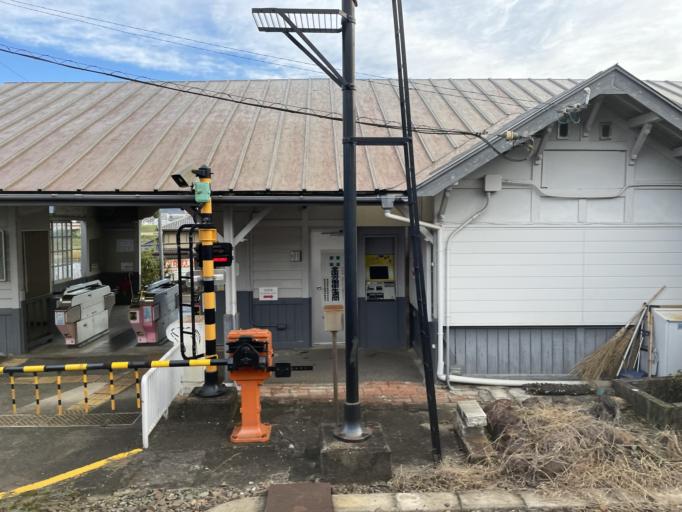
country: JP
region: Wakayama
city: Hashimoto
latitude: 34.2966
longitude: 135.5803
